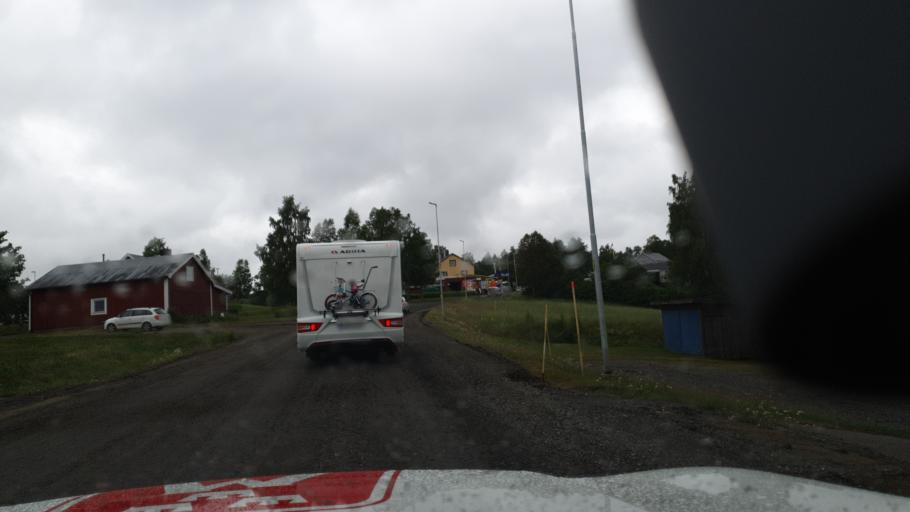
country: SE
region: Vaesterbotten
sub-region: Vannas Kommun
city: Vaennaes
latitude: 63.7675
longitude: 19.6224
